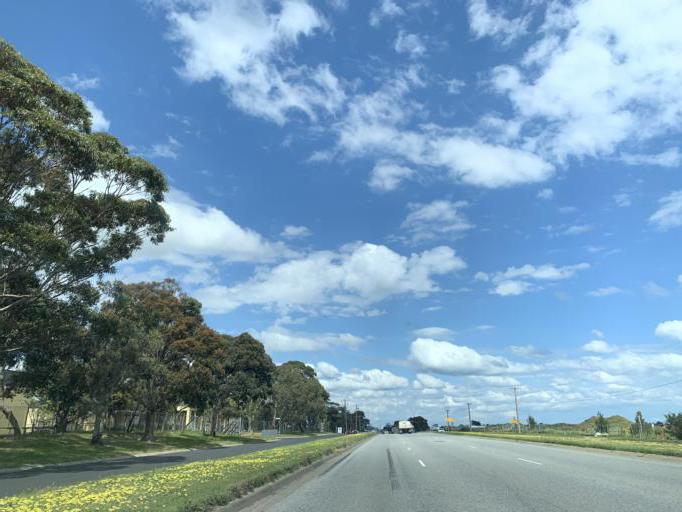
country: AU
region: Victoria
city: Heatherton
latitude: -37.9806
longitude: 145.1105
